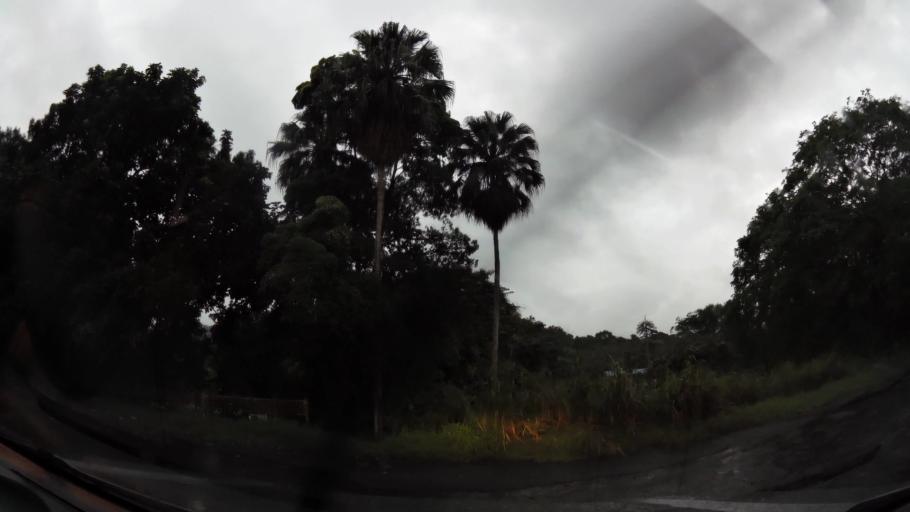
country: PA
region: Panama
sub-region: Distrito de Panama
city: Paraiso
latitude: 9.0302
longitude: -79.6276
